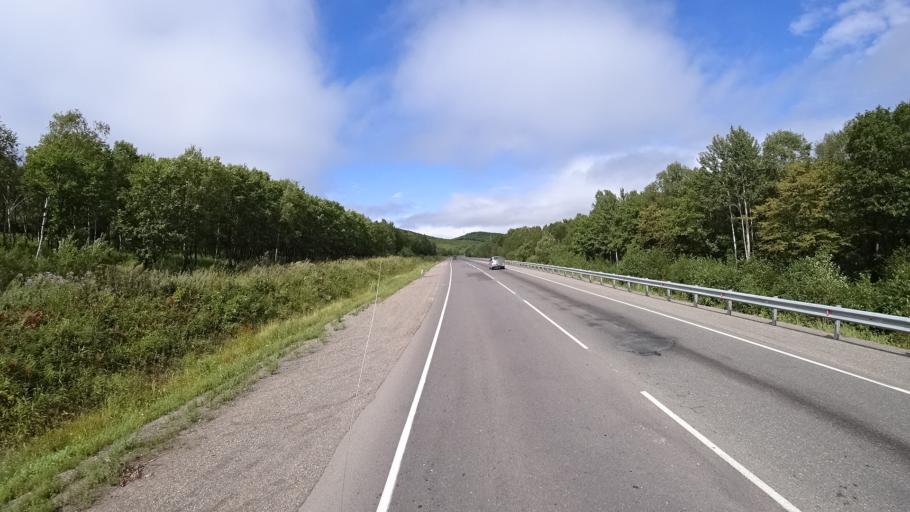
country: RU
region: Primorskiy
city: Lyalichi
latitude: 44.1121
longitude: 132.4199
